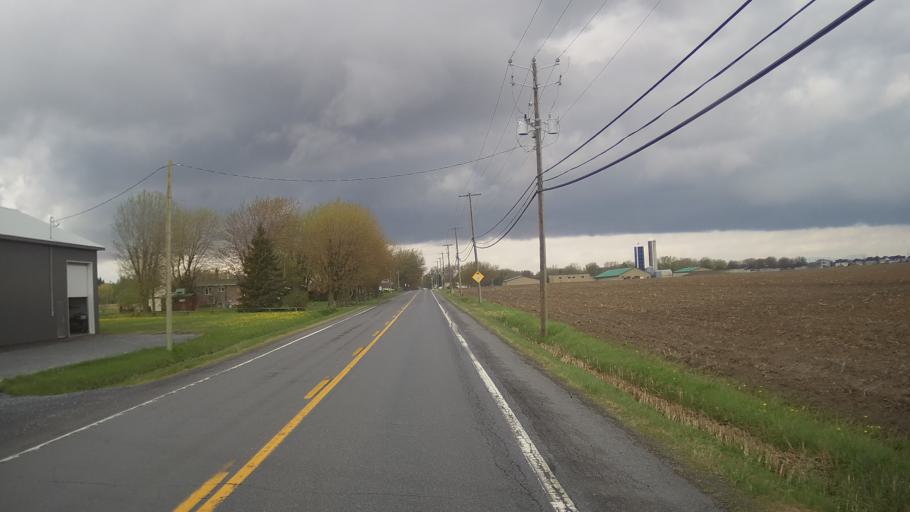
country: CA
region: Quebec
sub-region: Monteregie
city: Farnham
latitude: 45.3173
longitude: -73.0565
